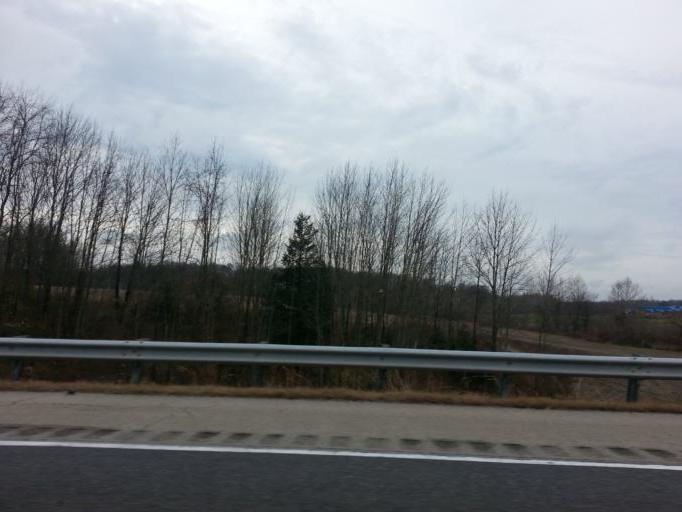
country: US
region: Indiana
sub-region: Ripley County
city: Batesville
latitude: 39.3136
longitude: -85.2271
